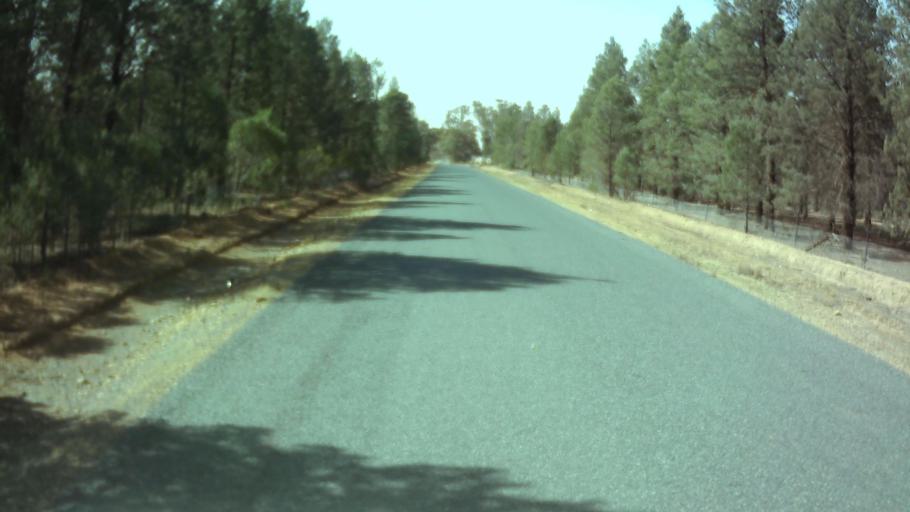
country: AU
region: New South Wales
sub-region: Weddin
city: Grenfell
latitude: -33.9012
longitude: 147.9207
